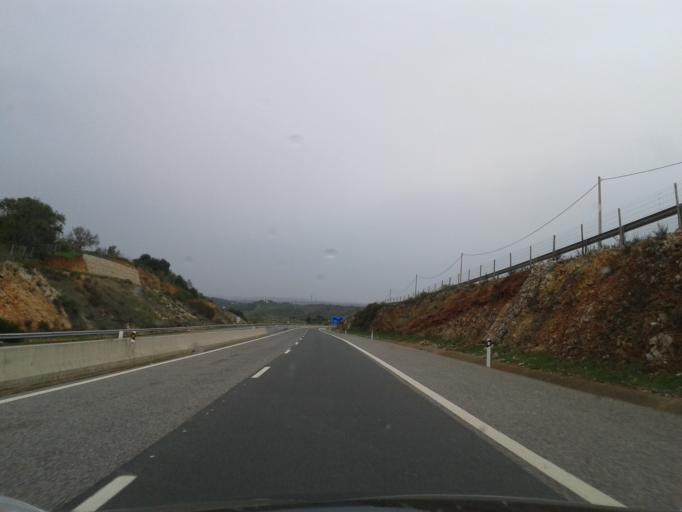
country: PT
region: Faro
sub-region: Portimao
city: Alvor
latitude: 37.1745
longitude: -8.6263
